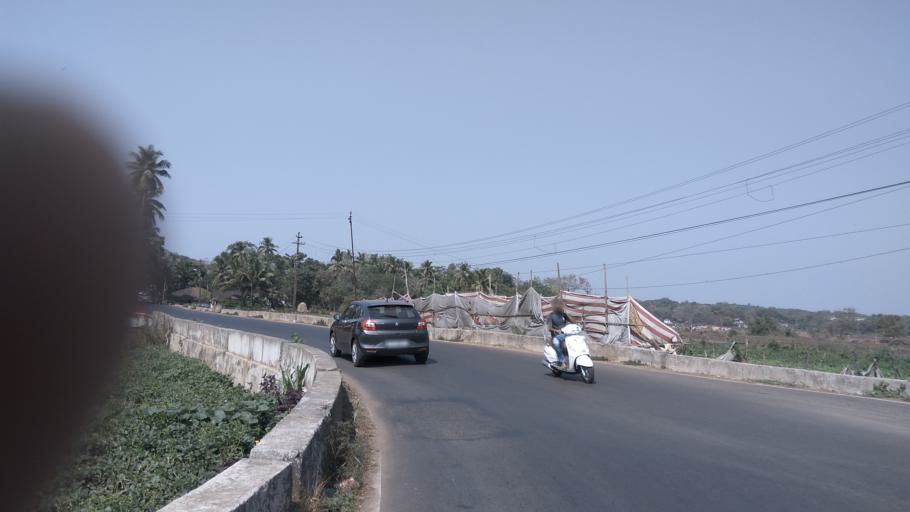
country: IN
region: Goa
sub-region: North Goa
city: Vagator
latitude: 15.5942
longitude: 73.7562
